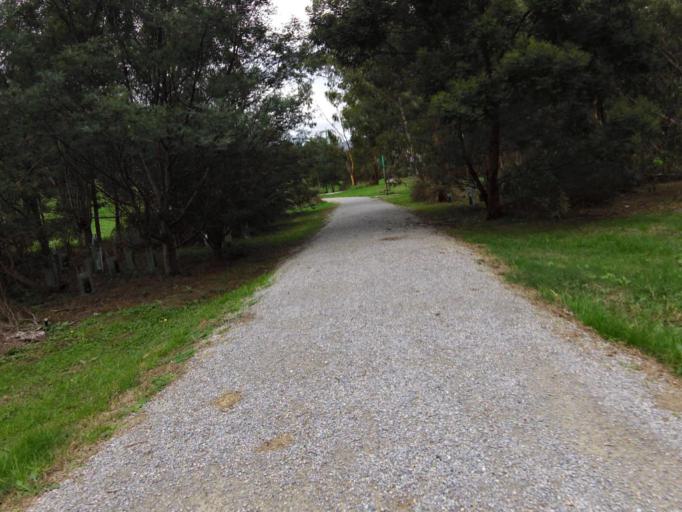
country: AU
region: Victoria
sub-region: Yarra Ranges
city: Mount Evelyn
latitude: -37.7815
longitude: 145.3624
